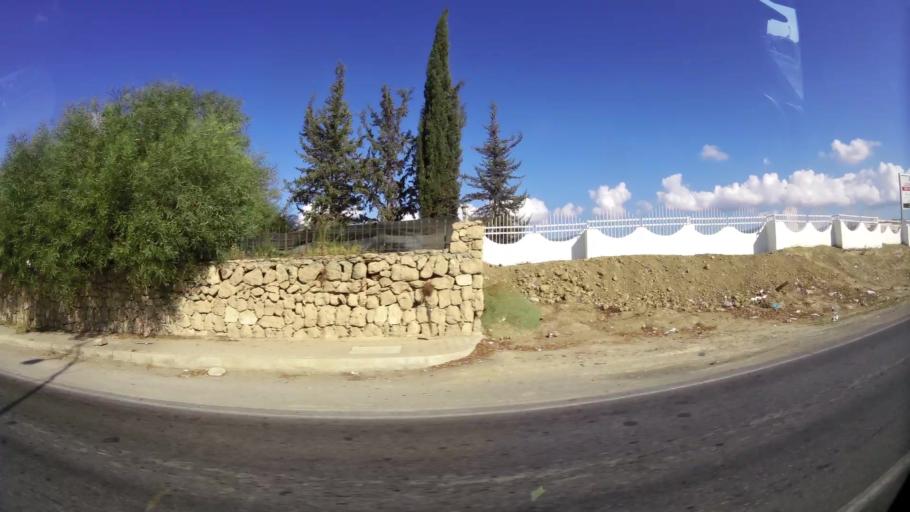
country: CY
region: Lefkosia
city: Nicosia
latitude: 35.2125
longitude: 33.3304
